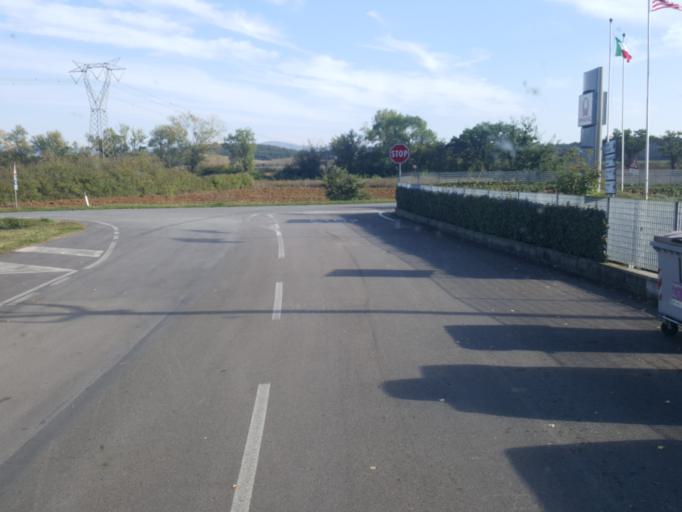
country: IT
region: Tuscany
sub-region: Provincia di Siena
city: Casole d'Elsa
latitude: 43.3688
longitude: 11.0631
